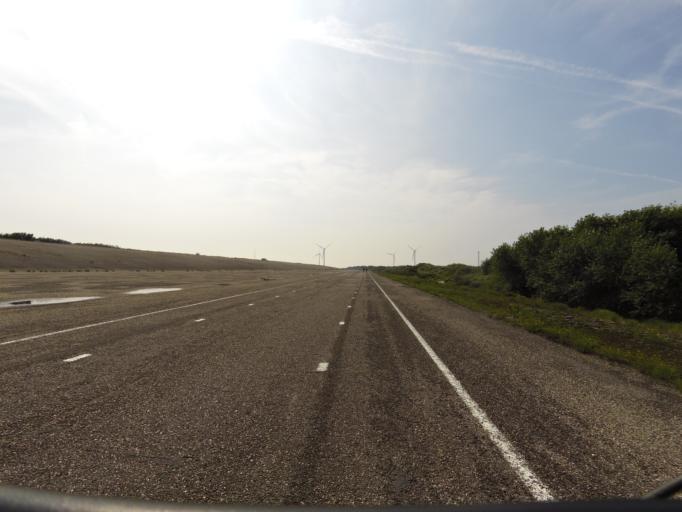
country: NL
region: Zeeland
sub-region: Gemeente Noord-Beveland
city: Kamperland
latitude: 51.6305
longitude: 3.6937
